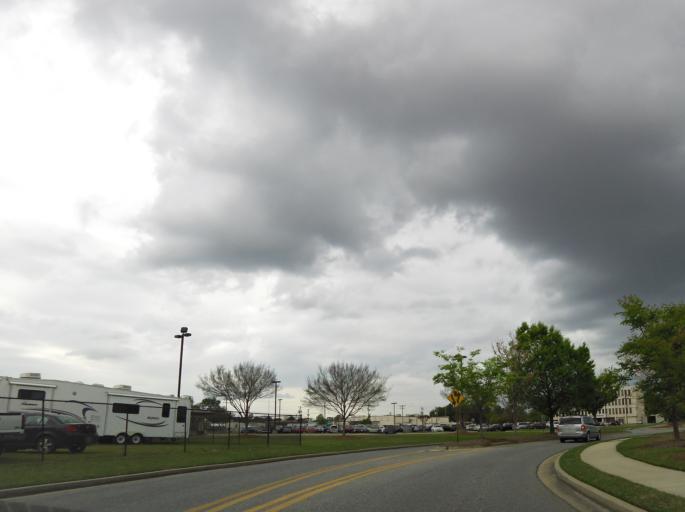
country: US
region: Georgia
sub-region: Houston County
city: Warner Robins
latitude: 32.6164
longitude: -83.6089
